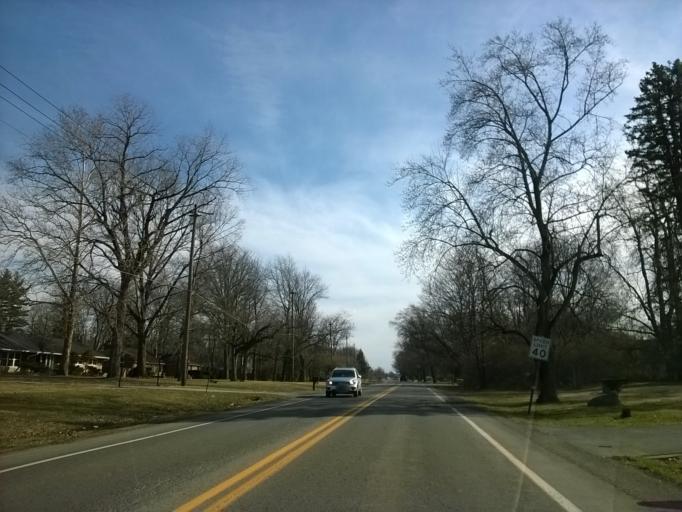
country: US
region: Indiana
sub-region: Marion County
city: Speedway
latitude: 39.8328
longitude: -86.2118
